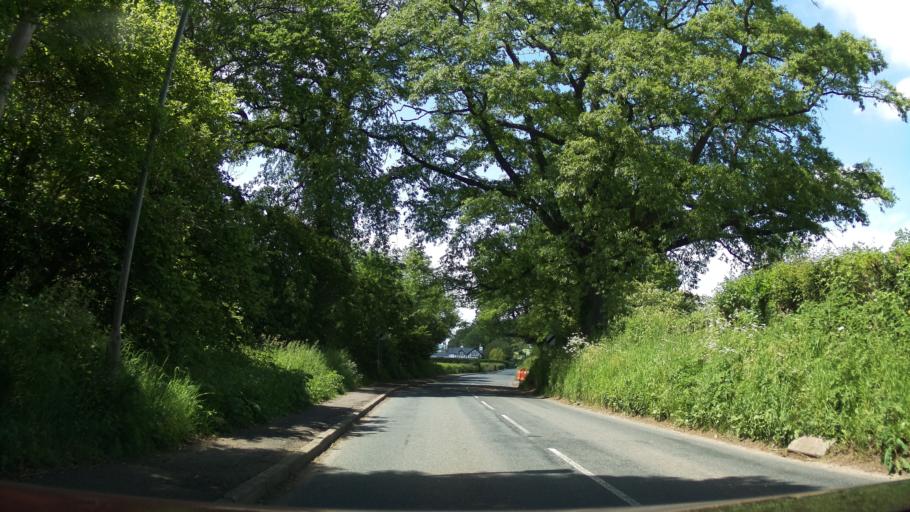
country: GB
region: Wales
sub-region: Monmouthshire
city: Monmouth
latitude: 51.8173
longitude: -2.7307
